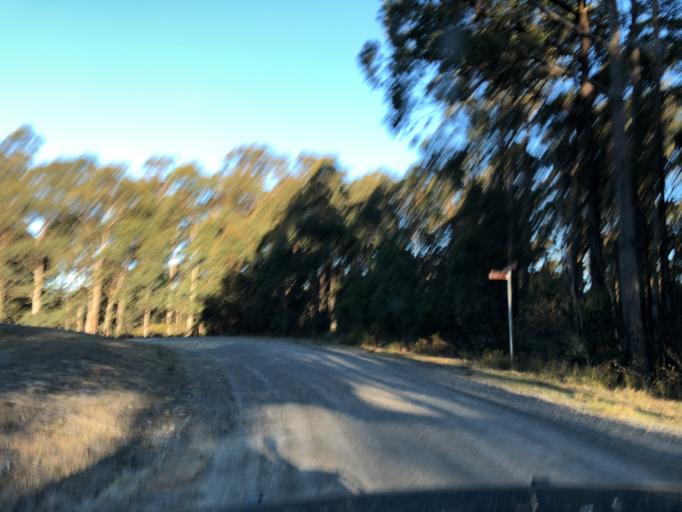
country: AU
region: Victoria
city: Brown Hill
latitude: -37.4851
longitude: 144.1963
